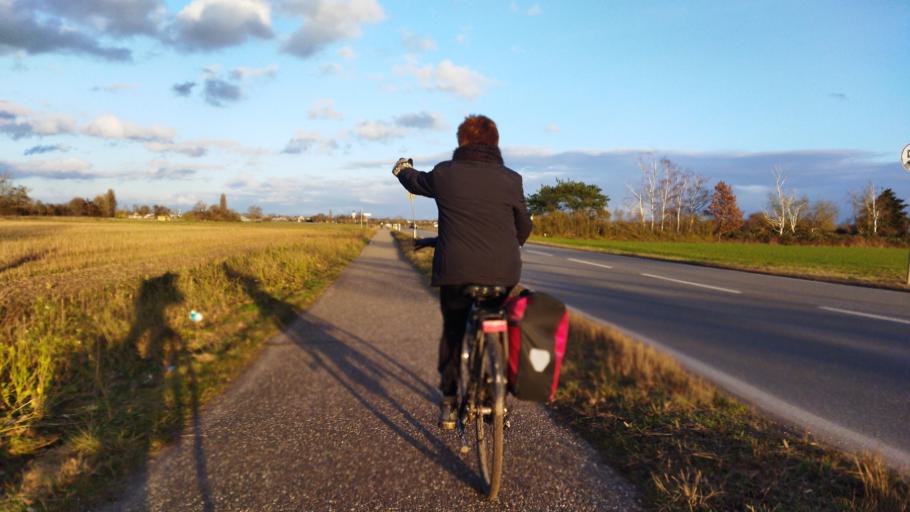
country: DE
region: Rheinland-Pfalz
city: Hassloch
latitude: 49.3591
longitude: 8.2846
